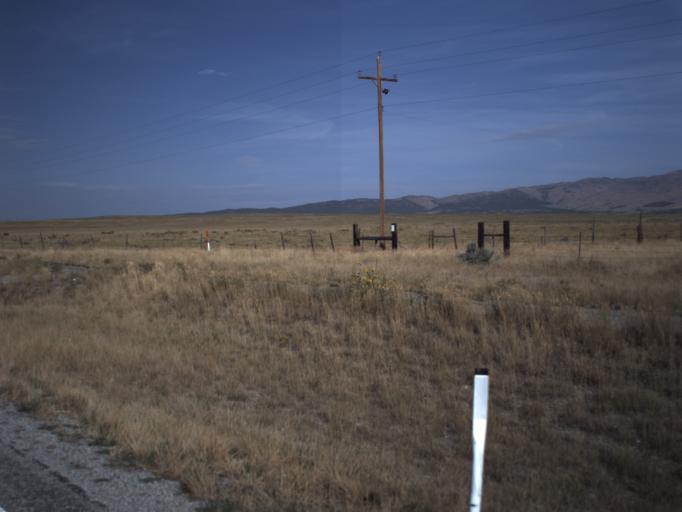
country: US
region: Idaho
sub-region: Oneida County
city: Malad City
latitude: 41.9655
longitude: -113.0388
